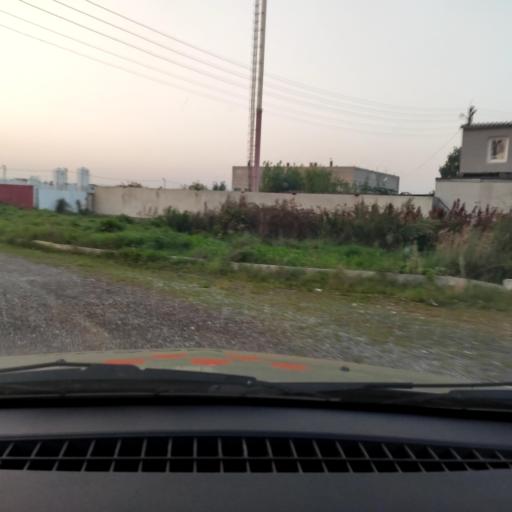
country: RU
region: Bashkortostan
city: Ufa
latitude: 54.8219
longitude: 56.1693
